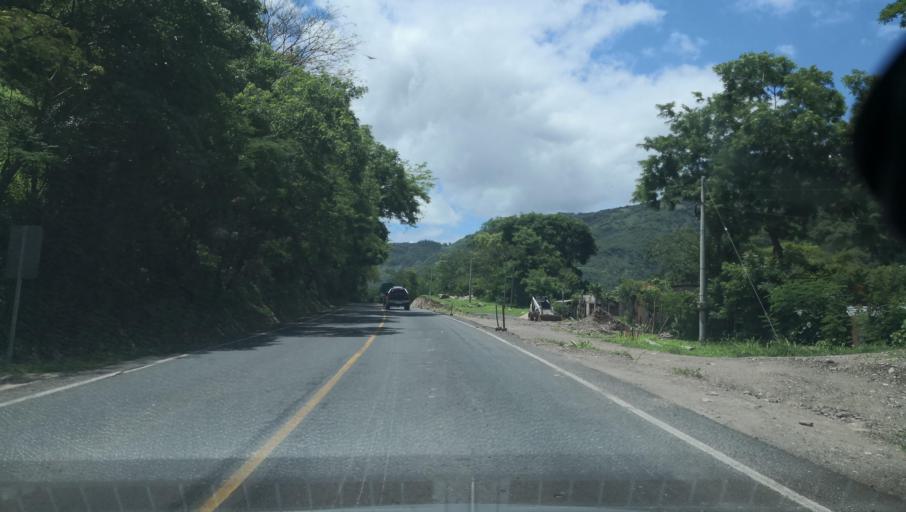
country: NI
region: Esteli
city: Condega
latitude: 13.2723
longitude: -86.3547
